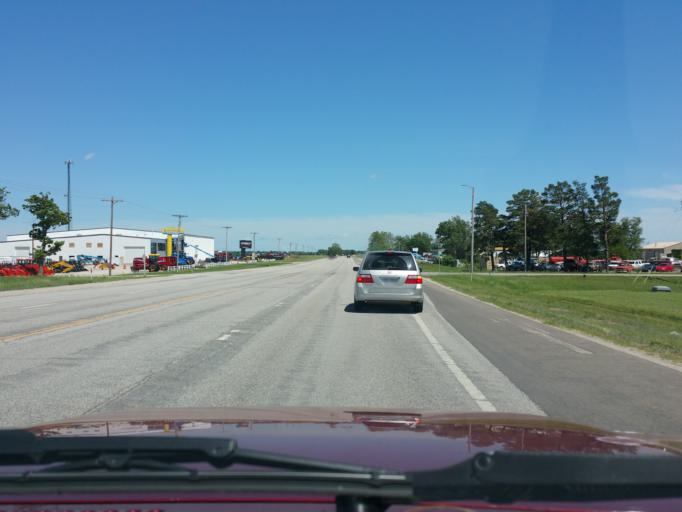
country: US
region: Kansas
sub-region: Pottawatomie County
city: Wamego
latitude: 39.2100
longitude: -96.2972
